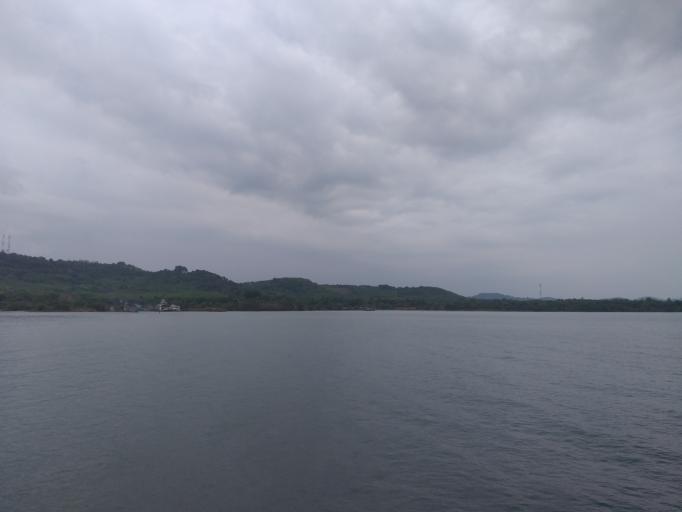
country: TH
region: Trat
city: Laem Ngop
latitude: 12.1788
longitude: 102.3008
